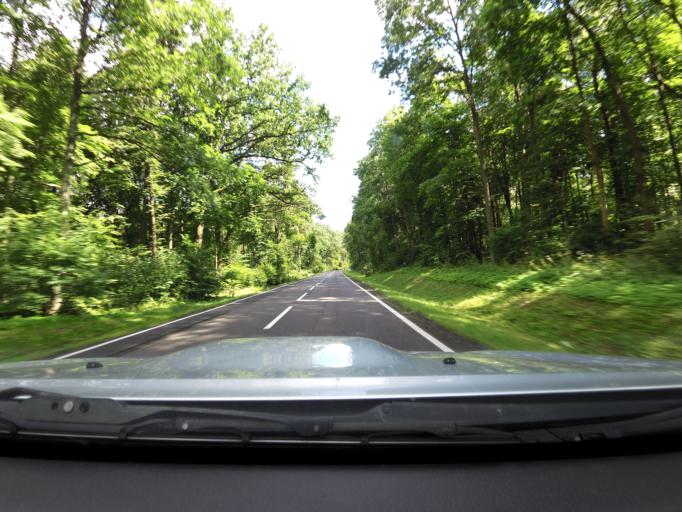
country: PL
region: Pomeranian Voivodeship
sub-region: Powiat kwidzynski
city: Ryjewo
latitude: 53.8108
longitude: 18.9698
